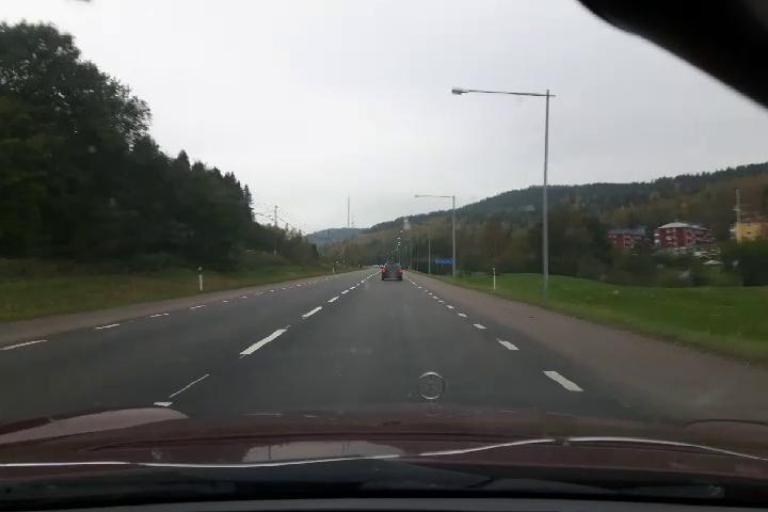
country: SE
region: Vaesternorrland
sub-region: OErnskoeldsviks Kommun
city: Ornskoldsvik
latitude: 63.2945
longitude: 18.6941
